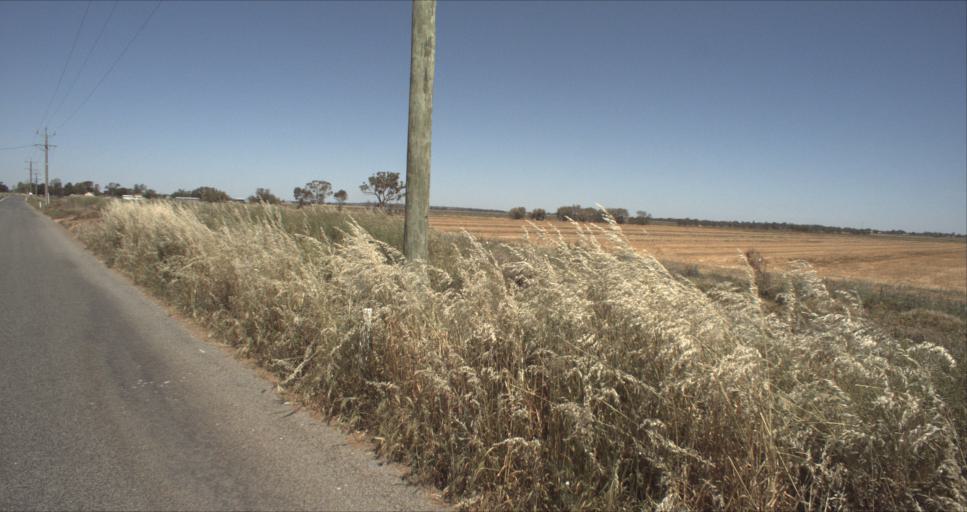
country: AU
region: New South Wales
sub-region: Leeton
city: Leeton
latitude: -34.5138
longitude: 146.4308
